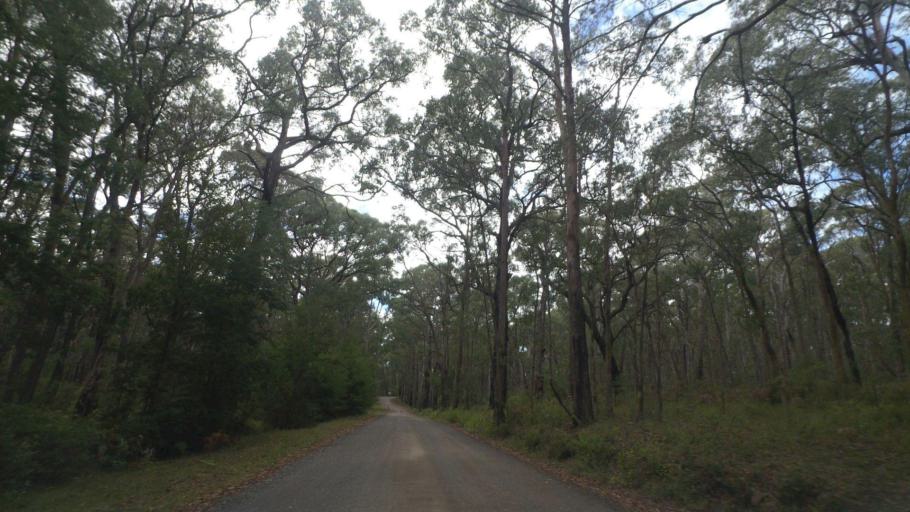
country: AU
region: Victoria
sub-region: Cardinia
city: Gembrook
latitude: -37.8894
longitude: 145.5849
